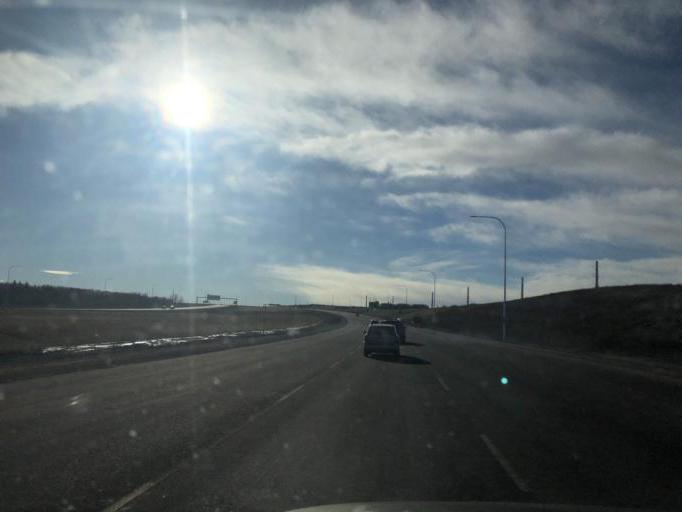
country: CA
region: Alberta
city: Calgary
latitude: 50.9903
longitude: -114.1678
